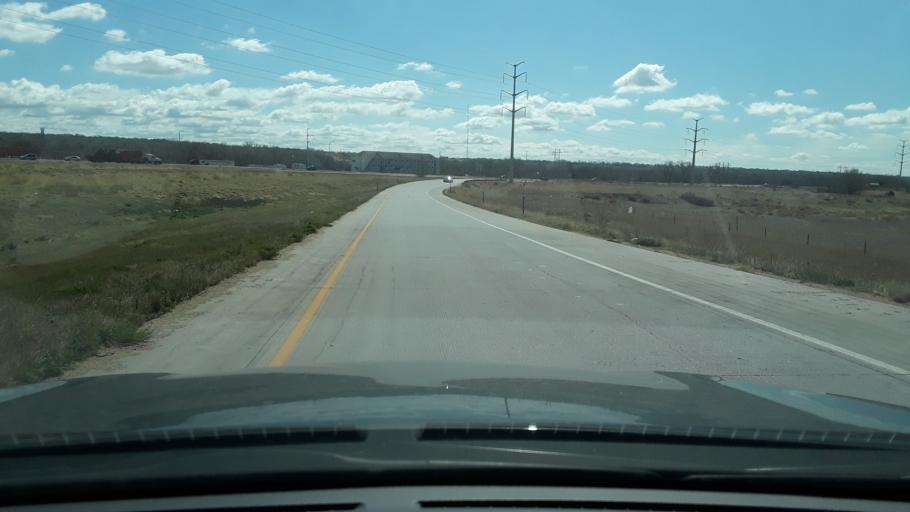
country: US
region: Colorado
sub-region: El Paso County
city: Security-Widefield
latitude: 38.7223
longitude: -104.7336
